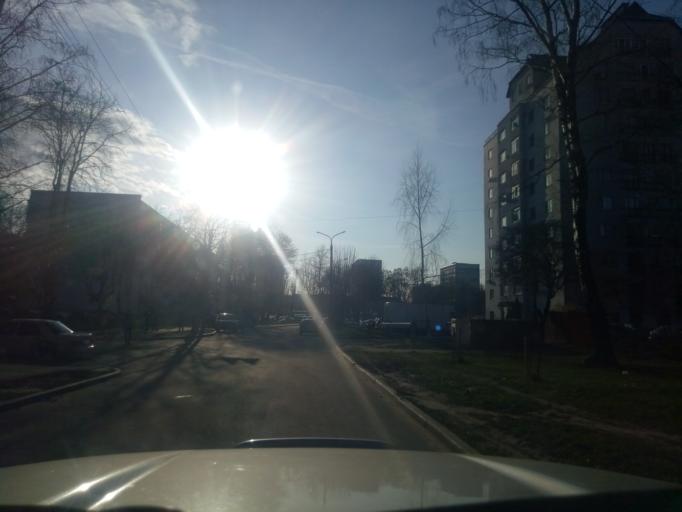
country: BY
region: Minsk
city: Novoye Medvezhino
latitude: 53.9139
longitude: 27.5007
